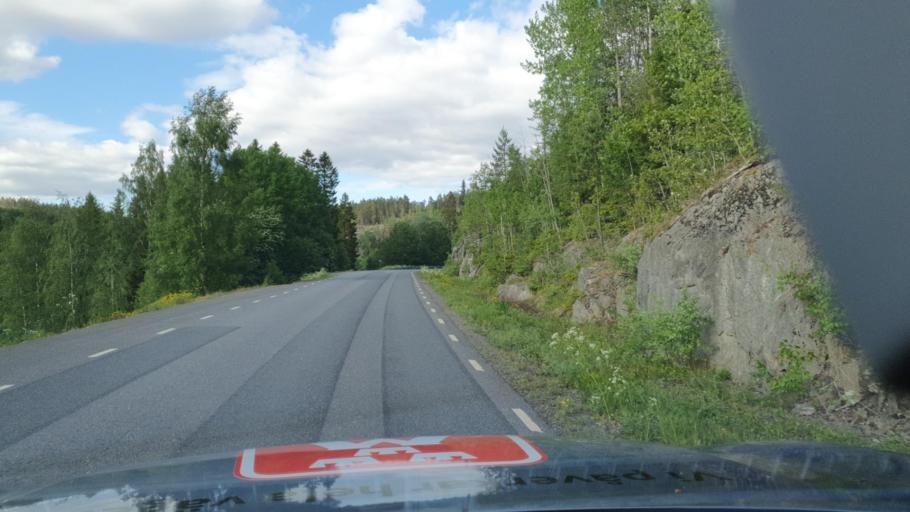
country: SE
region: Vaesternorrland
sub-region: Kramfors Kommun
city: Nordingra
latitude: 62.8139
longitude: 18.1591
